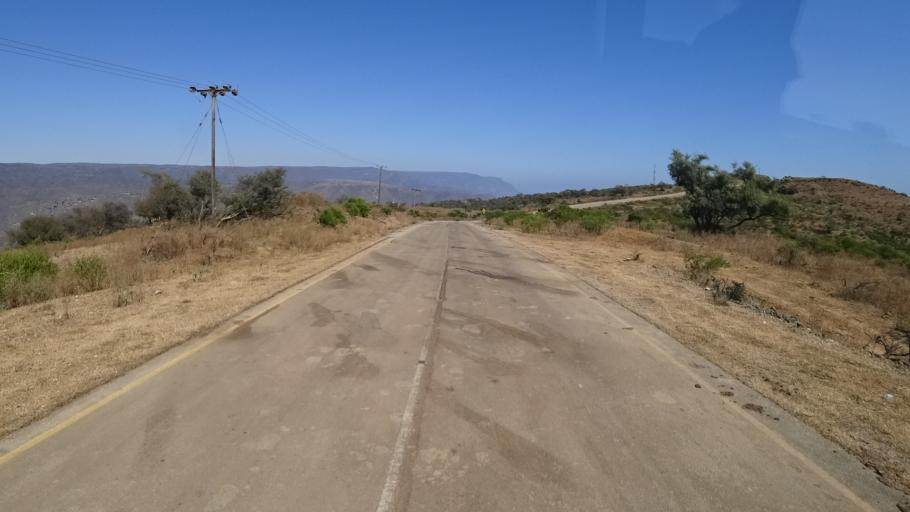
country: YE
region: Al Mahrah
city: Hawf
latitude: 16.7448
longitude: 53.3563
